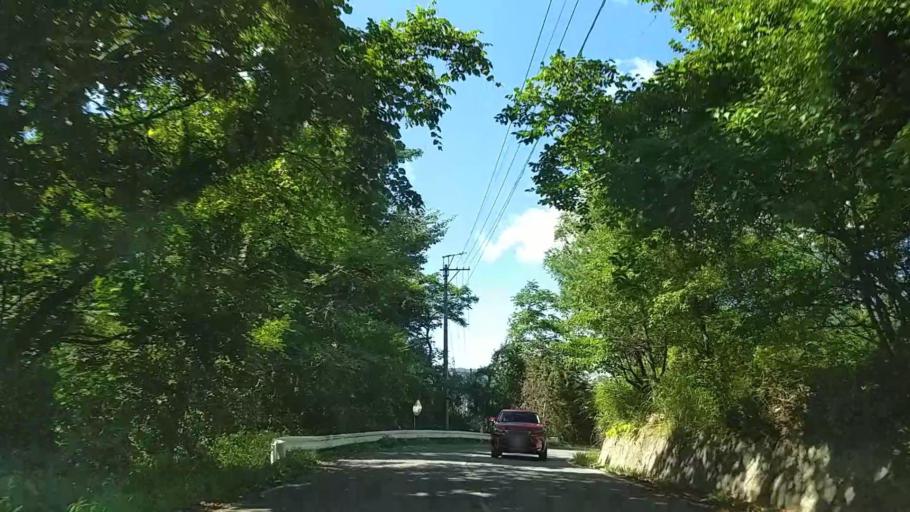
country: JP
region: Nagano
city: Matsumoto
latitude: 36.2085
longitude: 138.0937
